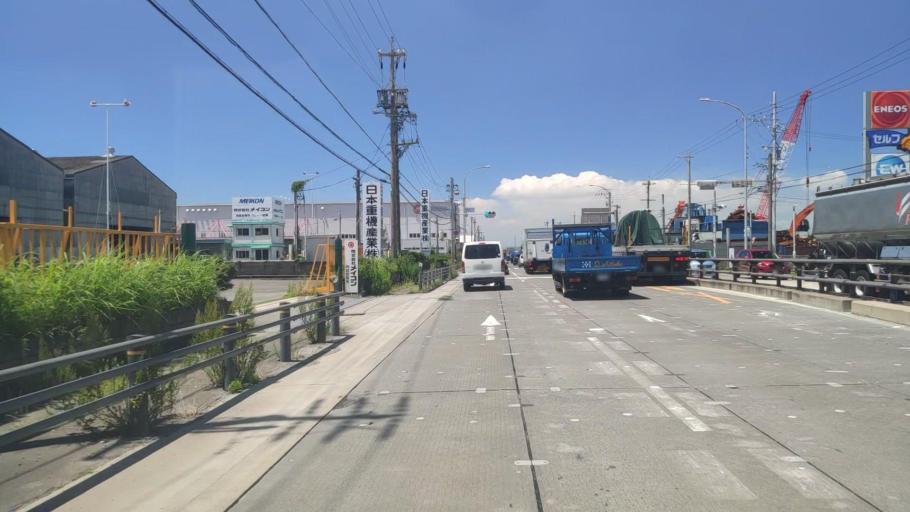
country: JP
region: Aichi
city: Kanie
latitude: 35.0772
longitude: 136.8048
